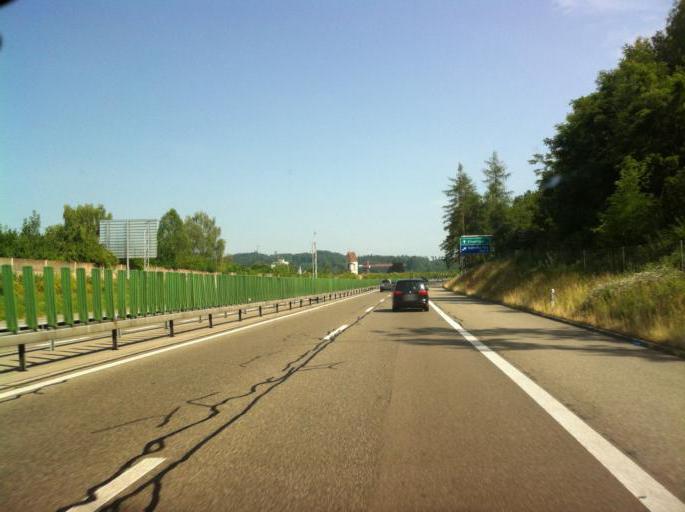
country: CH
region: Zurich
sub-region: Bezirk Winterthur
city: Wuelflingen (Kreis 6) / Oberfeld
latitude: 47.4961
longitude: 8.6957
